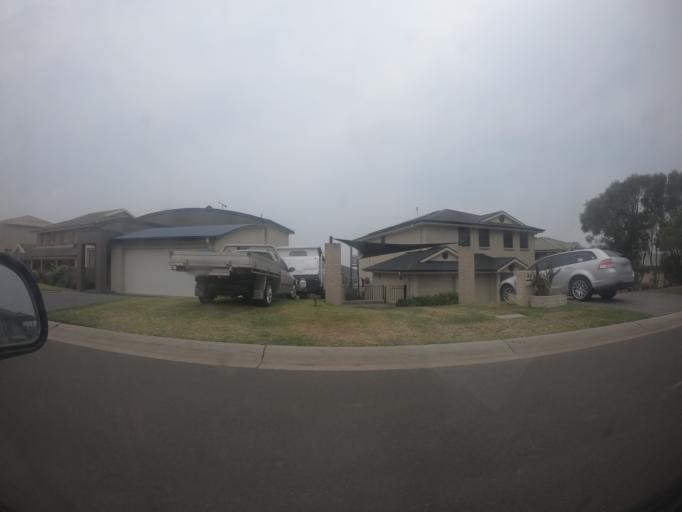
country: AU
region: New South Wales
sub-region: Shellharbour
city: Flinders
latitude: -34.5931
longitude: 150.8519
